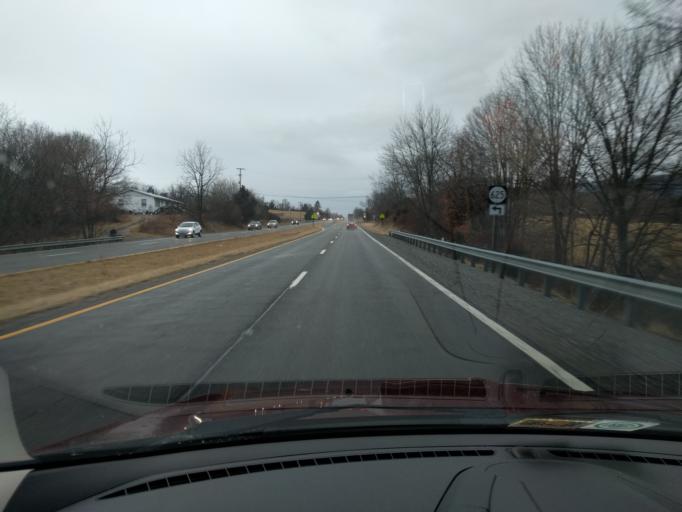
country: US
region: Virginia
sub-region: Giles County
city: Pembroke
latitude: 37.3093
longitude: -80.5779
